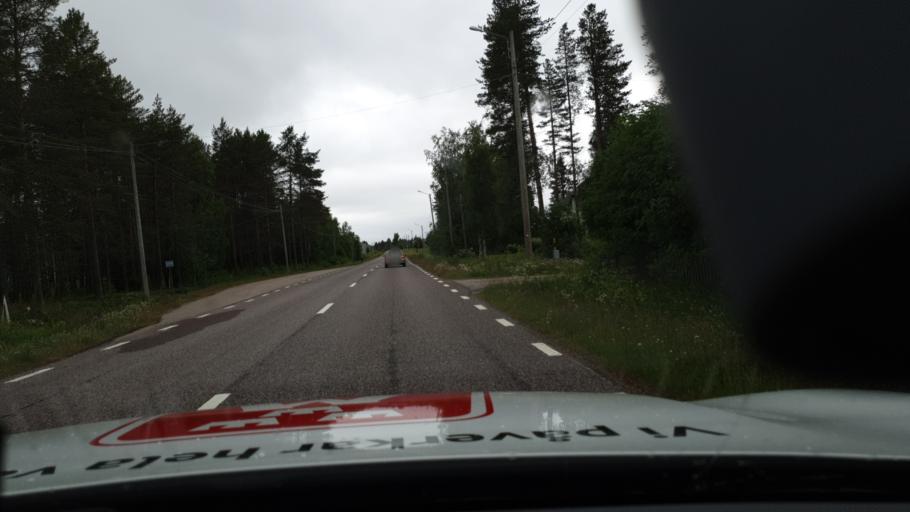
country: FI
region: Lapland
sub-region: Torniolaakso
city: Pello
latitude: 66.9791
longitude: 23.8011
